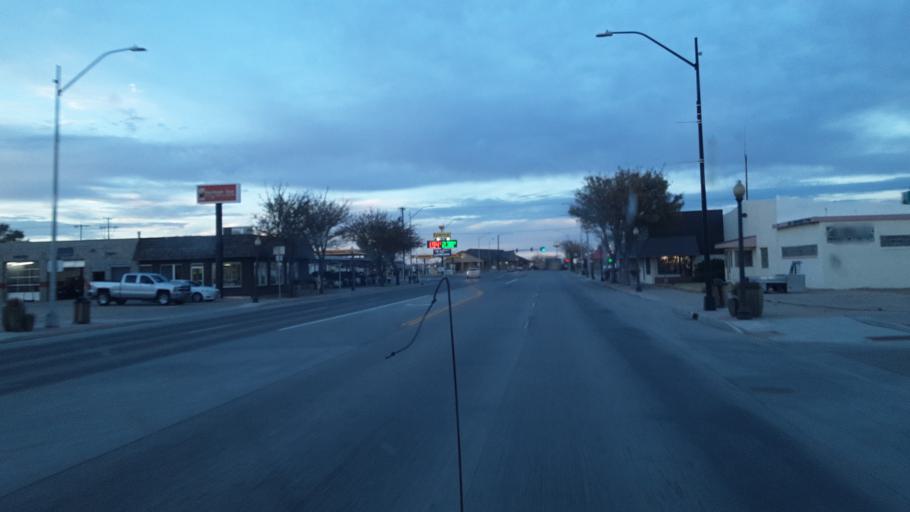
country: US
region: Colorado
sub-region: Prowers County
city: Lamar
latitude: 38.0942
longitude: -102.6196
